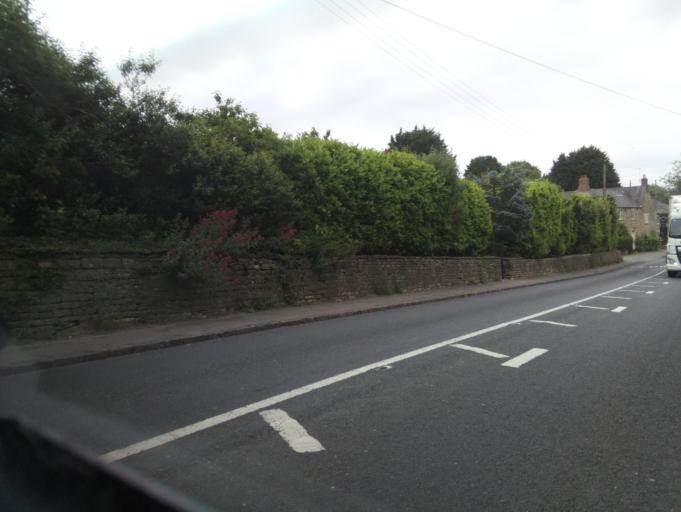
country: GB
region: England
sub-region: District of Rutland
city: Exton
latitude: 52.6692
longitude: -0.6348
